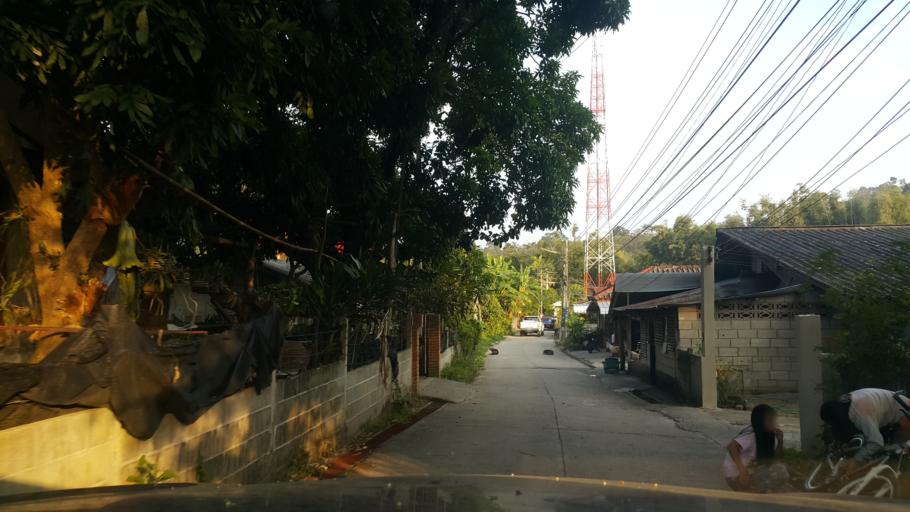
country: TH
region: Chiang Mai
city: Chiang Mai
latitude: 18.9009
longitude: 98.8828
